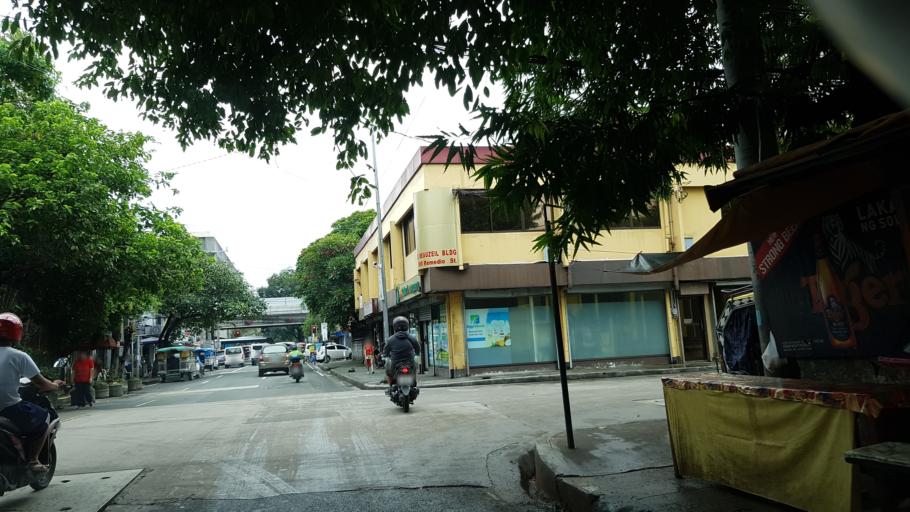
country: PH
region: Metro Manila
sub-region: City of Manila
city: Port Area
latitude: 14.5719
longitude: 120.9895
